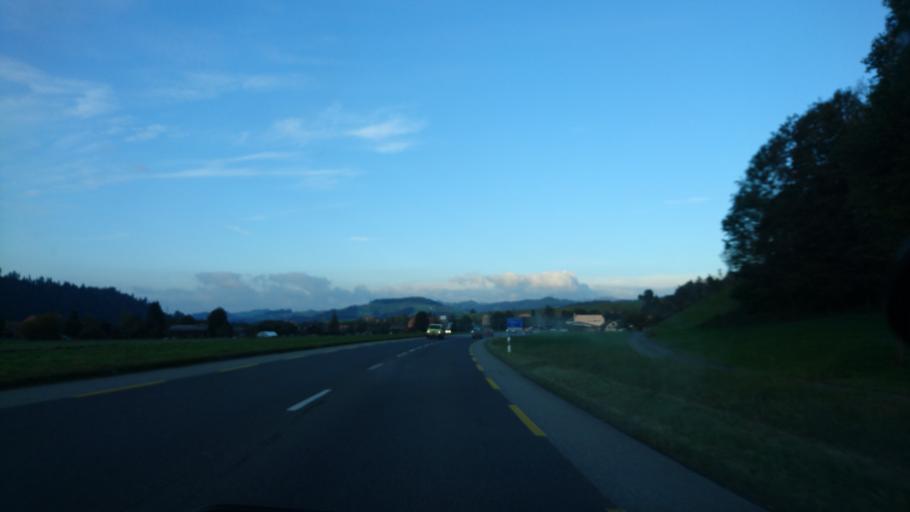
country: CH
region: Bern
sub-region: Emmental District
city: Signau
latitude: 46.9226
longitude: 7.7342
